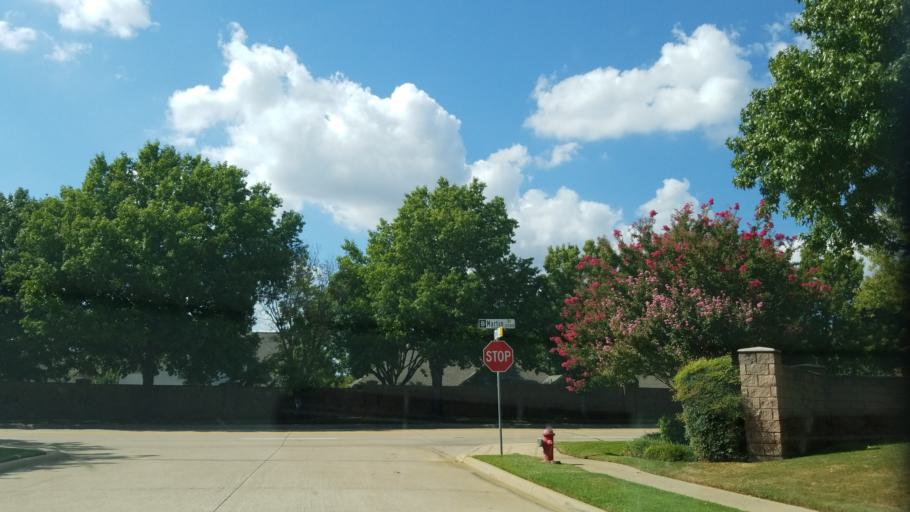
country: US
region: Texas
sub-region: Tarrant County
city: Bedford
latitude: 32.8459
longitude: -97.1187
